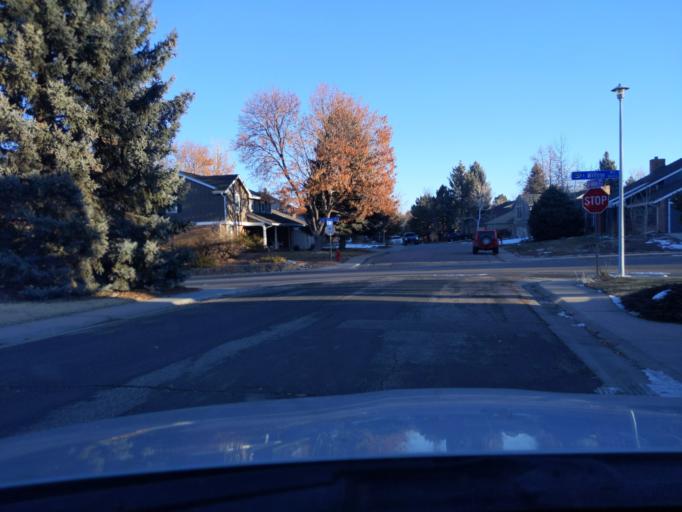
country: US
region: Colorado
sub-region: Arapahoe County
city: Centennial
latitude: 39.5755
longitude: -104.8893
